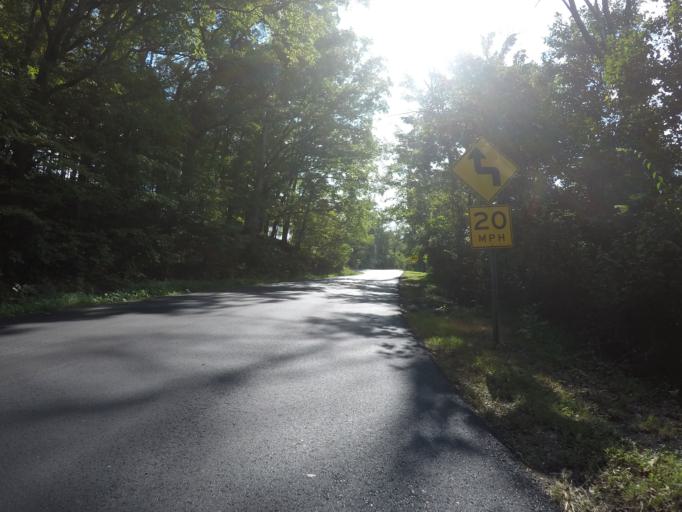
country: US
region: West Virginia
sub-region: Cabell County
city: Huntington
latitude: 38.3890
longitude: -82.4273
